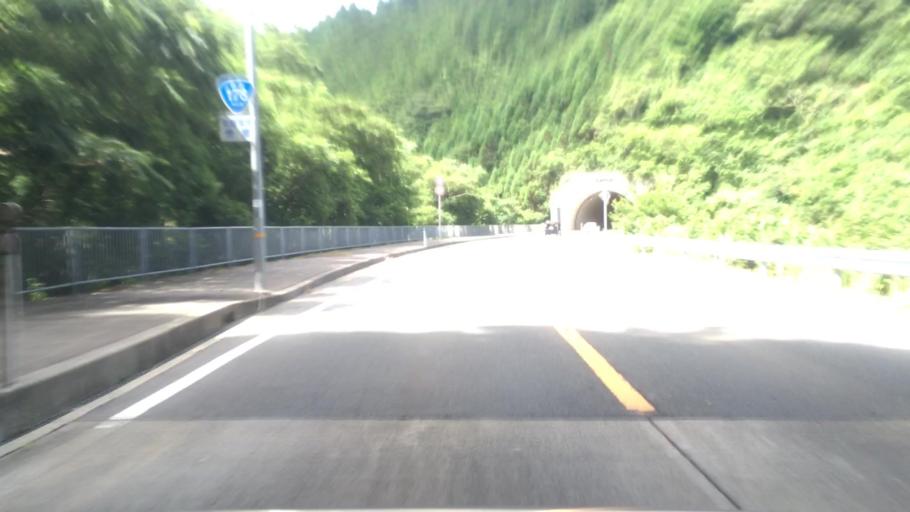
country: JP
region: Tottori
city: Tottori
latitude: 35.6180
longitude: 134.4161
